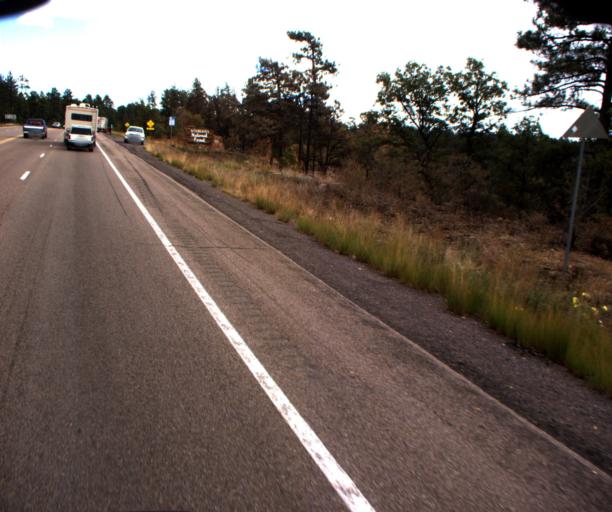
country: US
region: Arizona
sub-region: Navajo County
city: Heber-Overgaard
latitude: 34.3013
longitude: -110.9019
